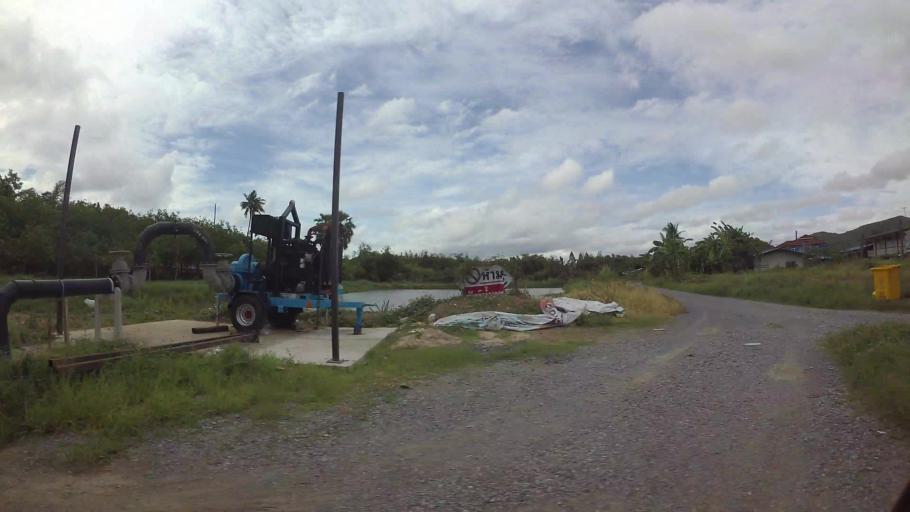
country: TH
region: Chon Buri
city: Sattahip
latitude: 12.7204
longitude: 100.9021
